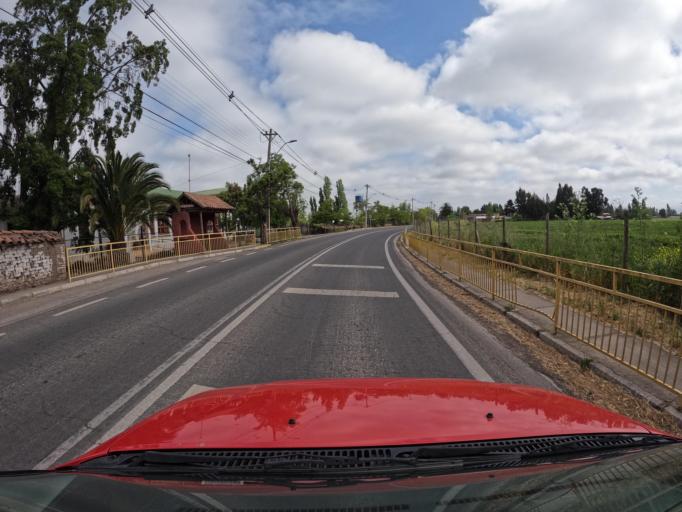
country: CL
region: O'Higgins
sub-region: Provincia de Colchagua
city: Santa Cruz
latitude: -34.6953
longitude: -71.3161
